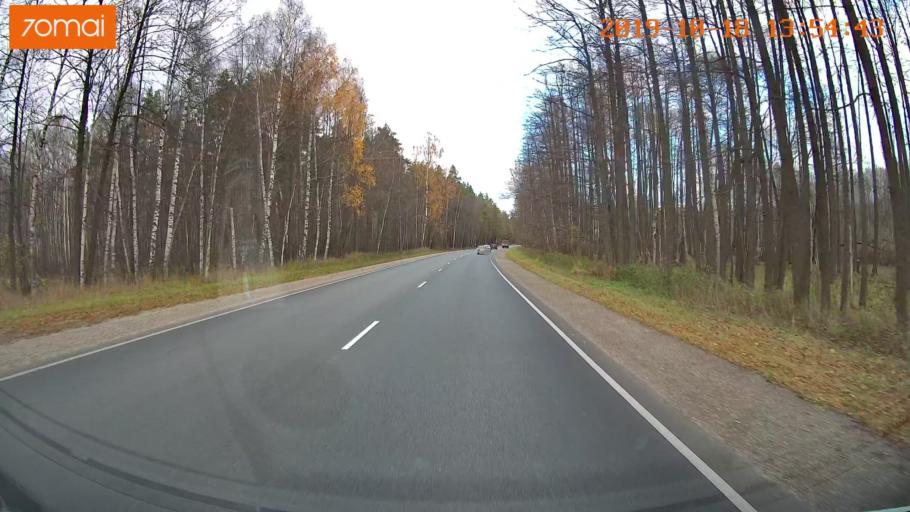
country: RU
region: Rjazan
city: Spas-Klepiki
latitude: 55.0458
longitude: 40.0135
